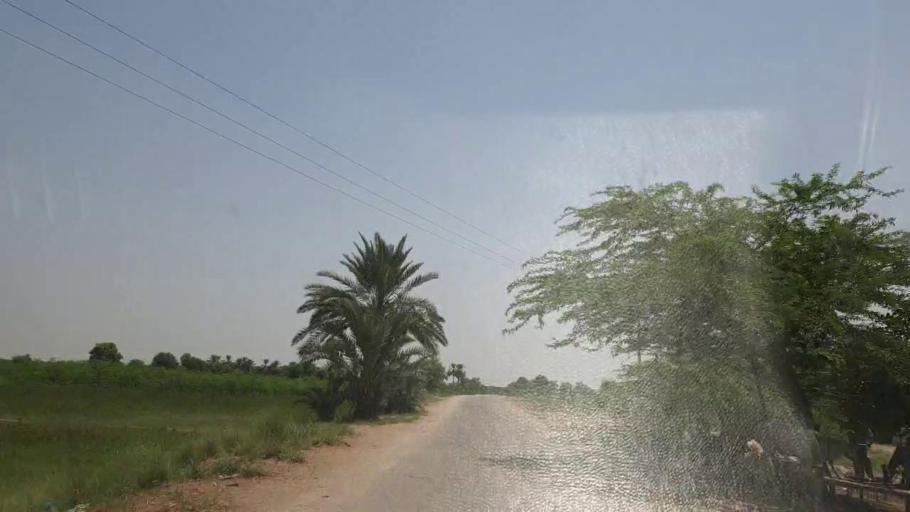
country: PK
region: Sindh
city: Bozdar
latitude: 27.2475
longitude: 68.6668
